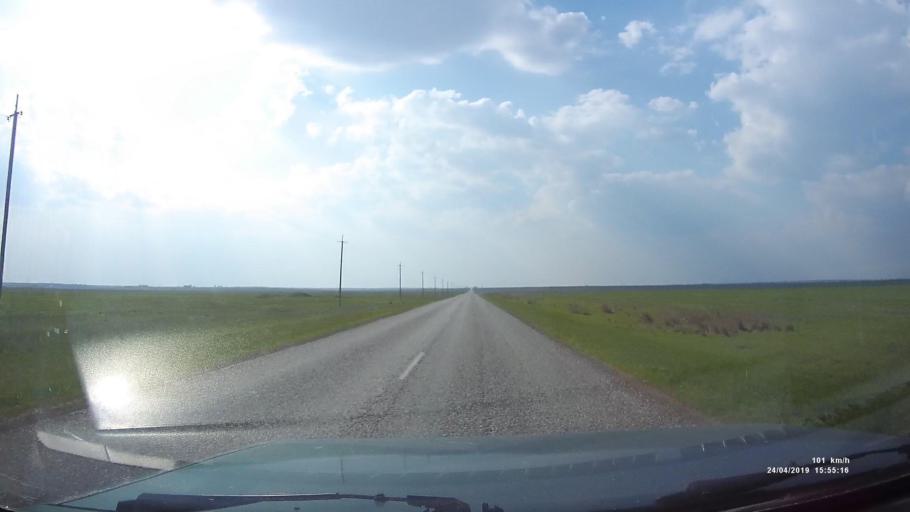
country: RU
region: Kalmykiya
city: Yashalta
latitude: 46.5892
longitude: 42.5528
